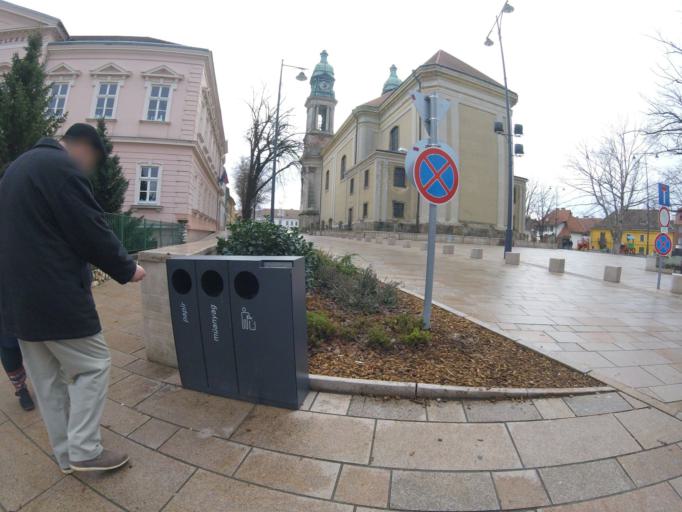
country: HU
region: Veszprem
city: Papa
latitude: 47.3319
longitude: 17.4656
